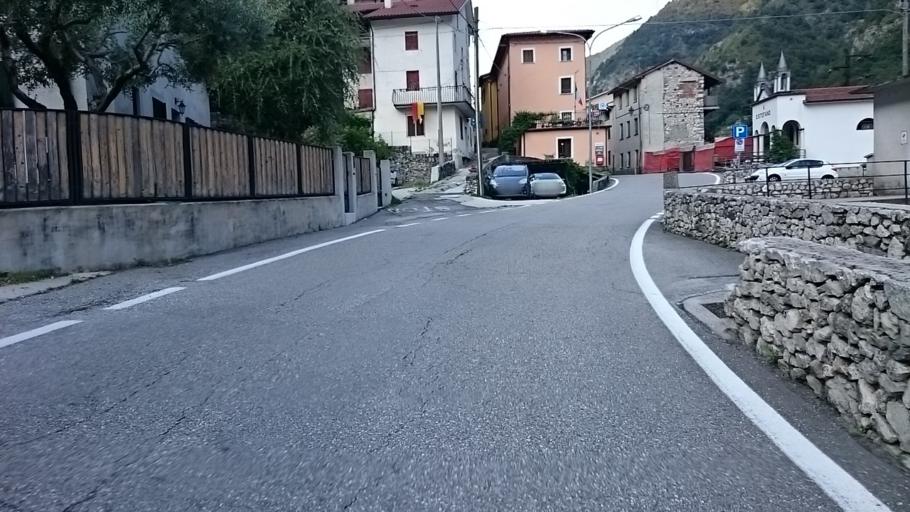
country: IT
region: Veneto
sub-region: Provincia di Vicenza
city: Valstagna
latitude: 45.8795
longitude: 11.6777
